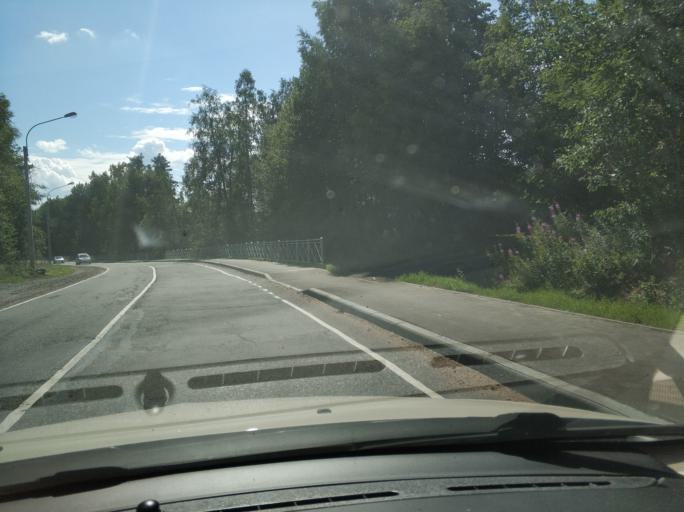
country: RU
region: Leningrad
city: Osel'ki
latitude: 60.2121
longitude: 30.5560
